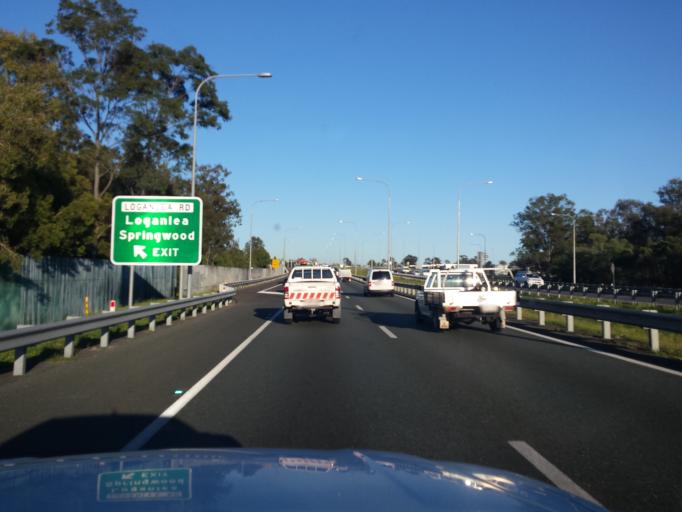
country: AU
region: Queensland
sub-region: Logan
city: Slacks Creek
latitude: -27.6660
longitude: 153.1451
